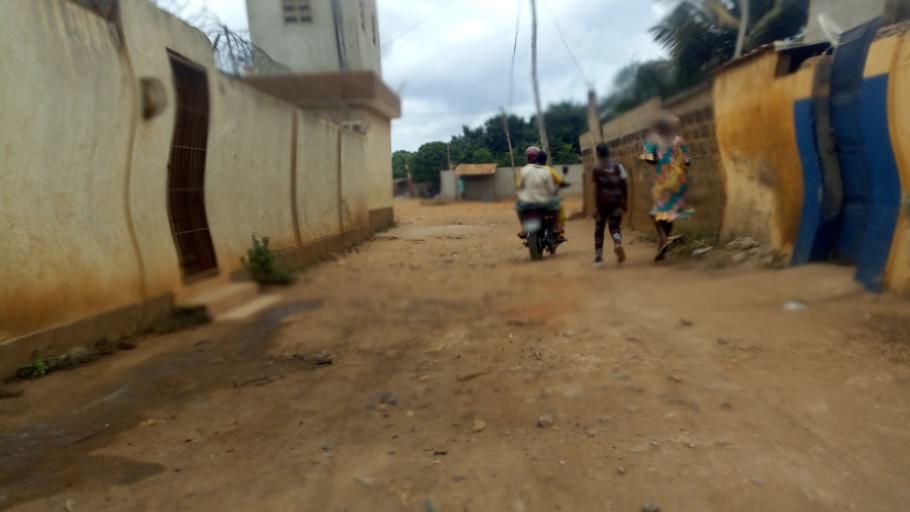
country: TG
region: Maritime
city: Lome
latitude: 6.2272
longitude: 1.1872
